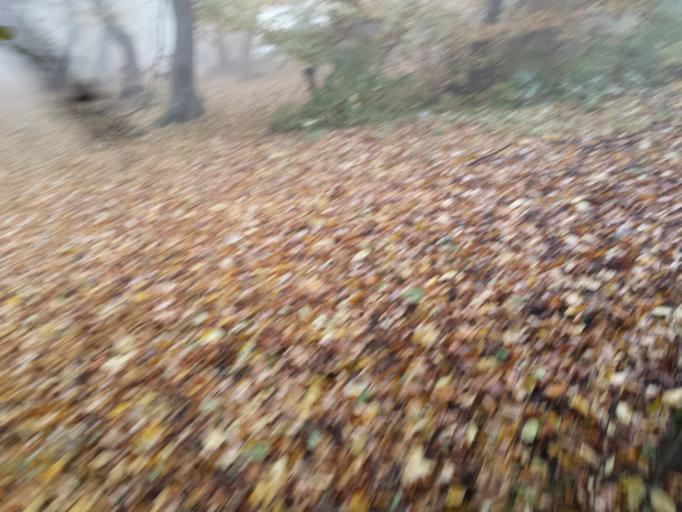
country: RO
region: Cluj
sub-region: Comuna Baciu
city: Baciu
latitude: 46.7692
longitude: 23.5391
